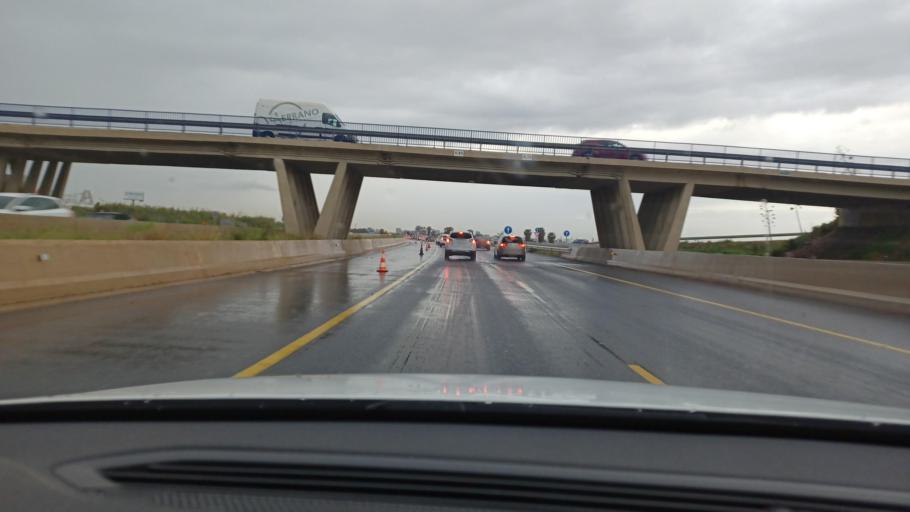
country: ES
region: Valencia
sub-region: Provincia de Valencia
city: Meliana
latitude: 39.5091
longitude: -0.3250
